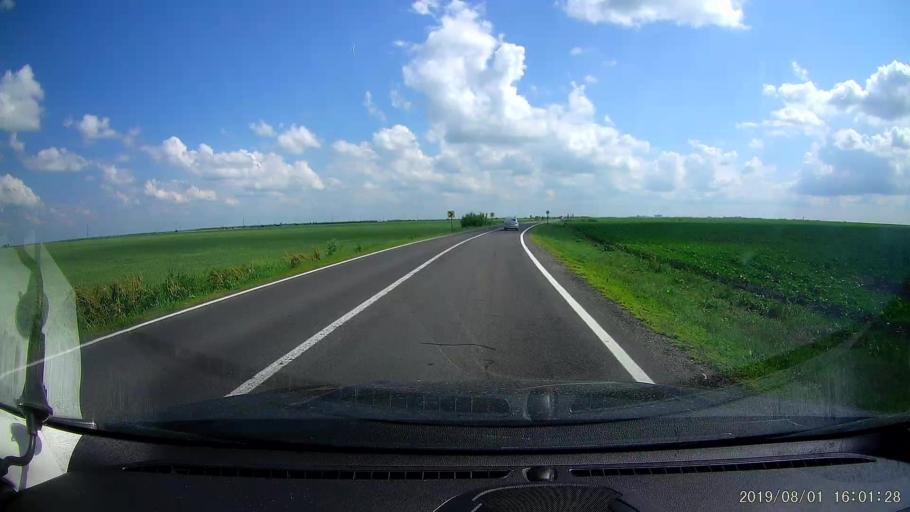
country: RO
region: Ialomita
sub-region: Comuna Ciulnita
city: Ciulnita
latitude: 44.5079
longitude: 27.3903
